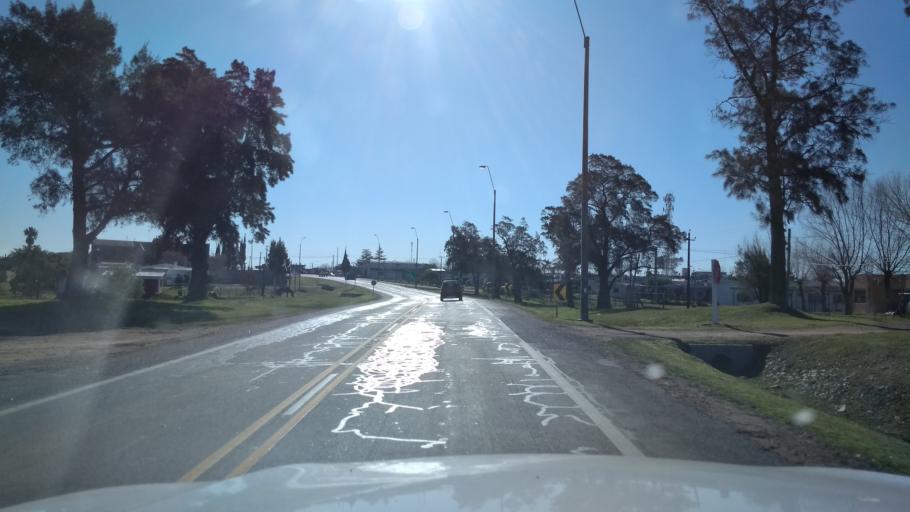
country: UY
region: Canelones
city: San Jacinto
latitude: -34.5495
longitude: -55.8698
